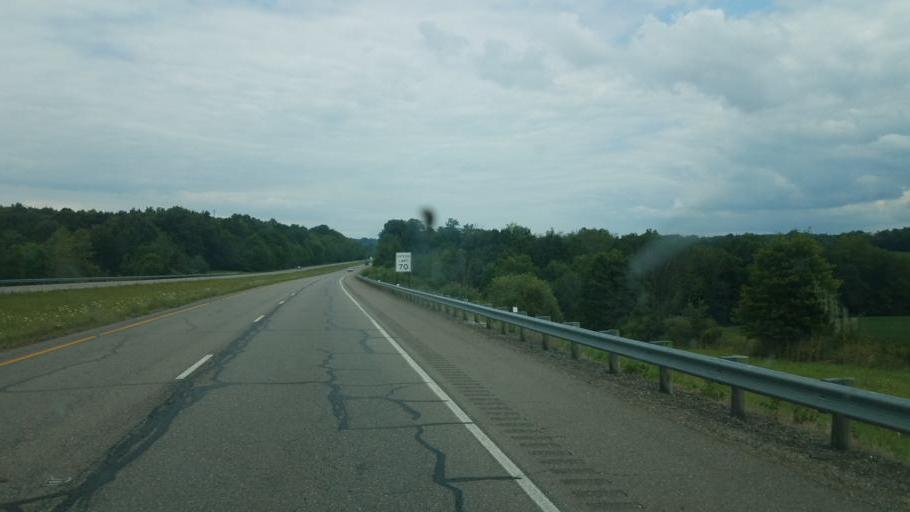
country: US
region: Ohio
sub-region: Columbiana County
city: Lisbon
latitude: 40.8009
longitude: -80.7455
